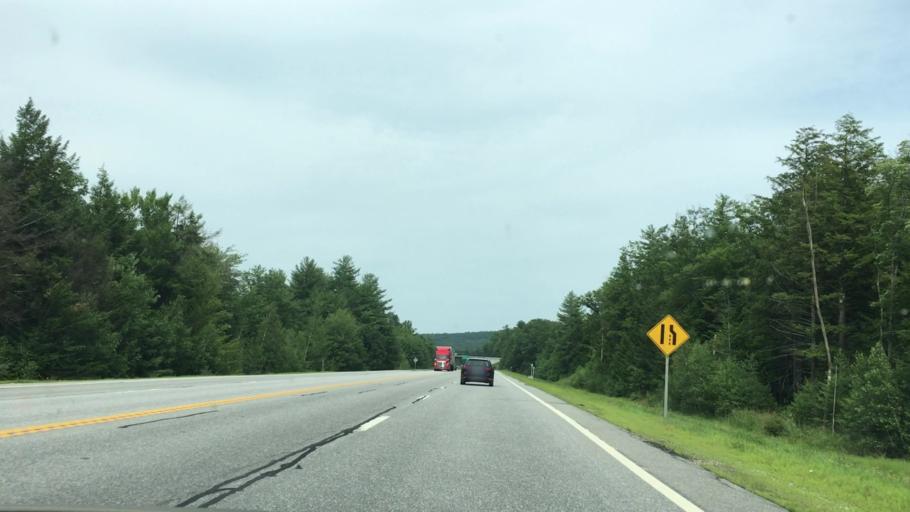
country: US
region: New Hampshire
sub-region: Hillsborough County
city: Hillsborough
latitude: 43.1193
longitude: -71.9072
